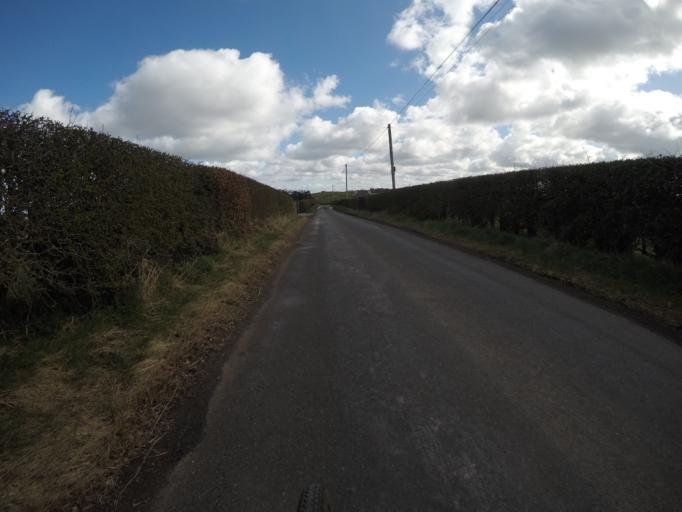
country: GB
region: Scotland
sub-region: South Ayrshire
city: Dundonald
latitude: 55.5892
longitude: -4.5850
